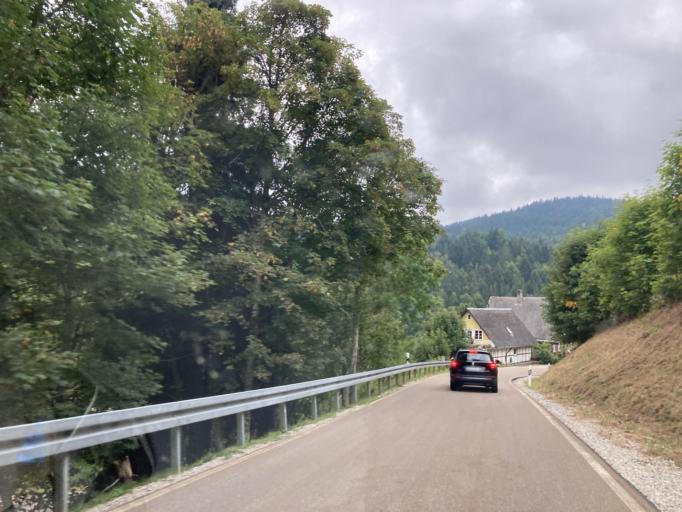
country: DE
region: Baden-Wuerttemberg
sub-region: Freiburg Region
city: Muenstertal/Schwarzwald
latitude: 47.7990
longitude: 7.7586
